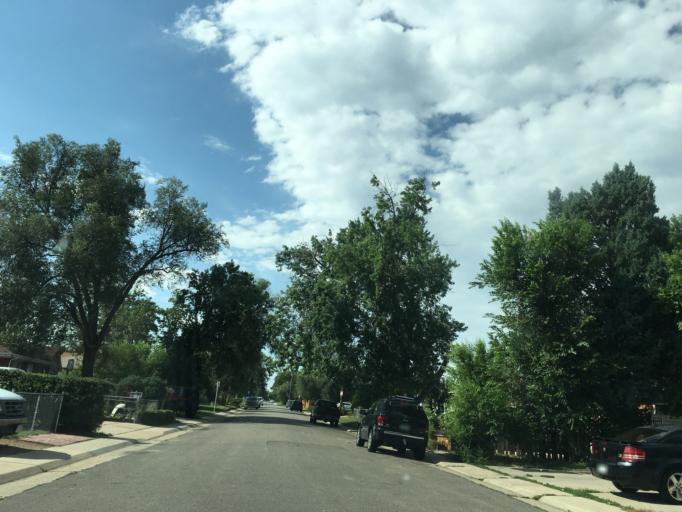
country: US
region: Colorado
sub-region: Jefferson County
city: Lakewood
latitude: 39.7021
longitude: -105.0380
